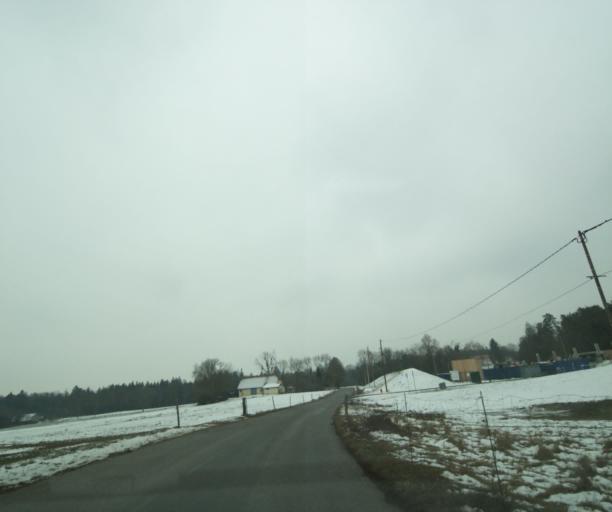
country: FR
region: Rhone-Alpes
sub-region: Departement de la Haute-Savoie
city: Reignier-Esery
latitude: 46.1220
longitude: 6.2892
